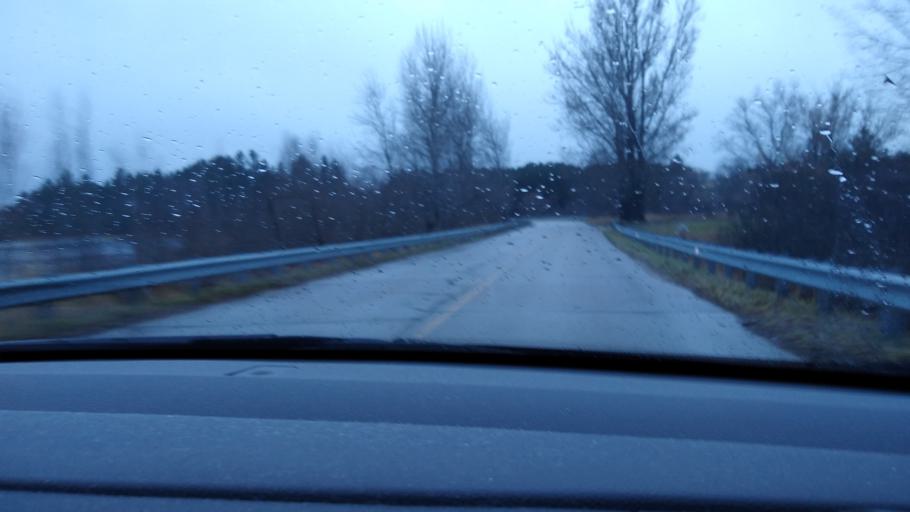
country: US
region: Michigan
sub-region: Wexford County
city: Cadillac
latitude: 44.1863
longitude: -85.3955
